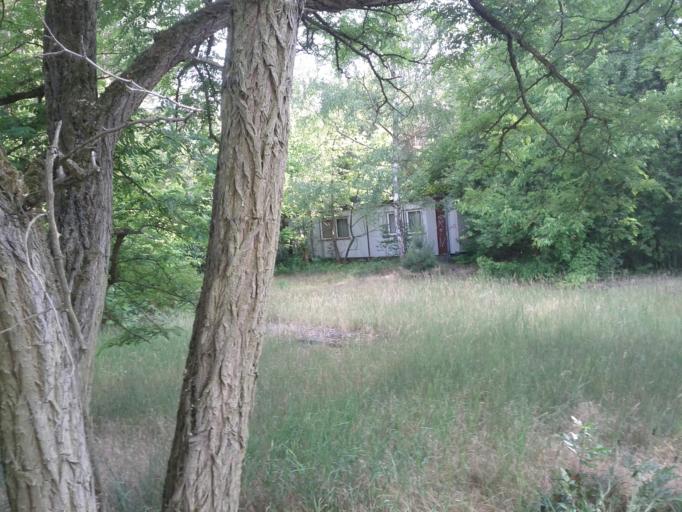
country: DE
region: Berlin
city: Friedrichshagen
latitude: 52.4502
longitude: 13.6138
